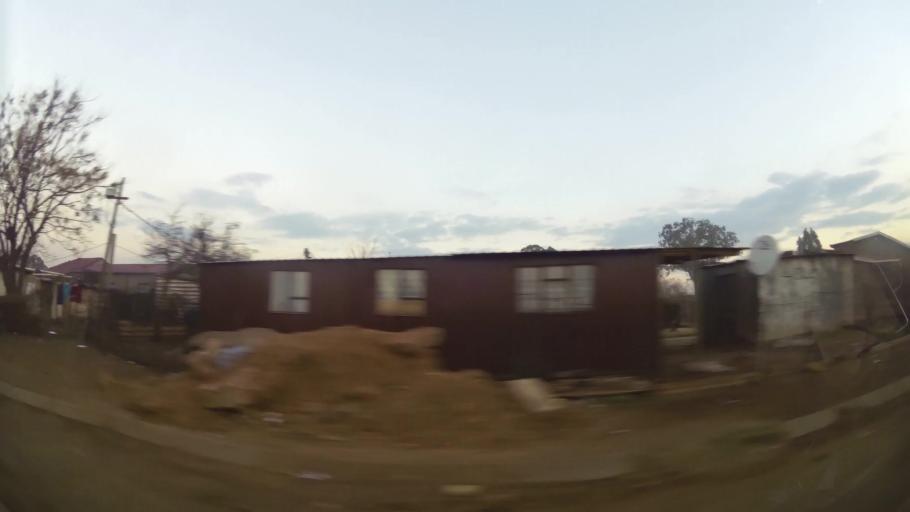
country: ZA
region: Gauteng
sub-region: City of Johannesburg Metropolitan Municipality
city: Orange Farm
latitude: -26.5486
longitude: 27.8574
